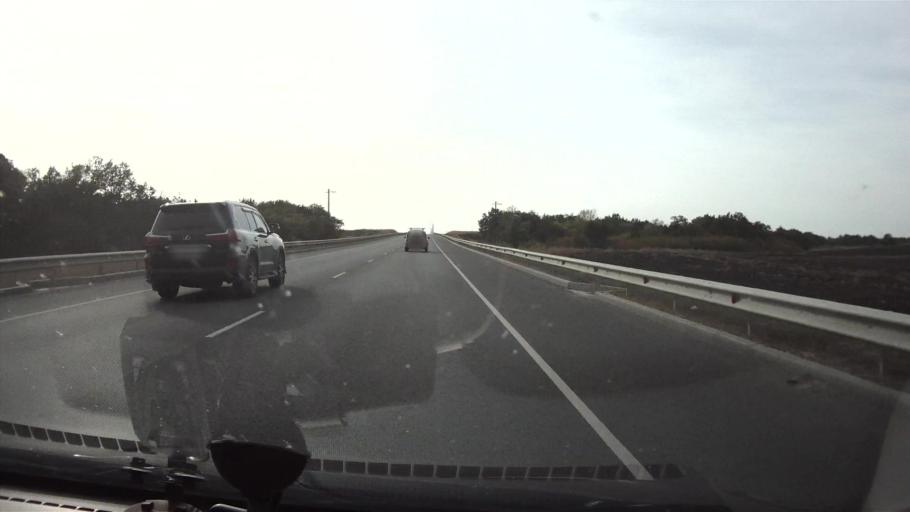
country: RU
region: Saratov
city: Yelshanka
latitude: 51.8309
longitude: 46.4523
